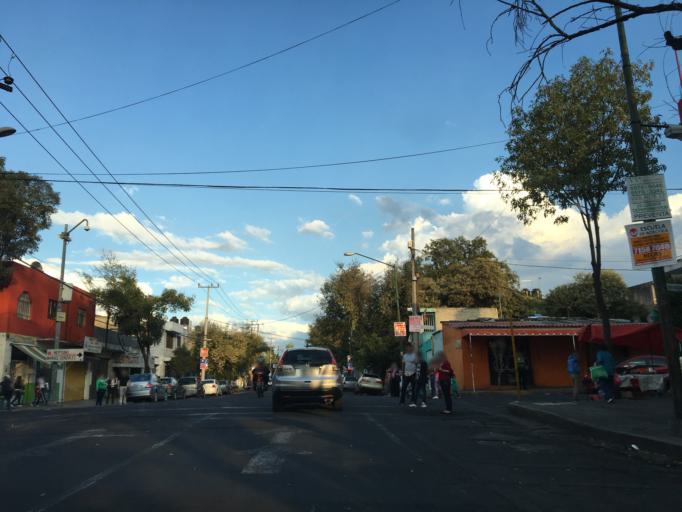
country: MX
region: Mexico City
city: Cuauhtemoc
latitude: 19.4586
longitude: -99.1432
